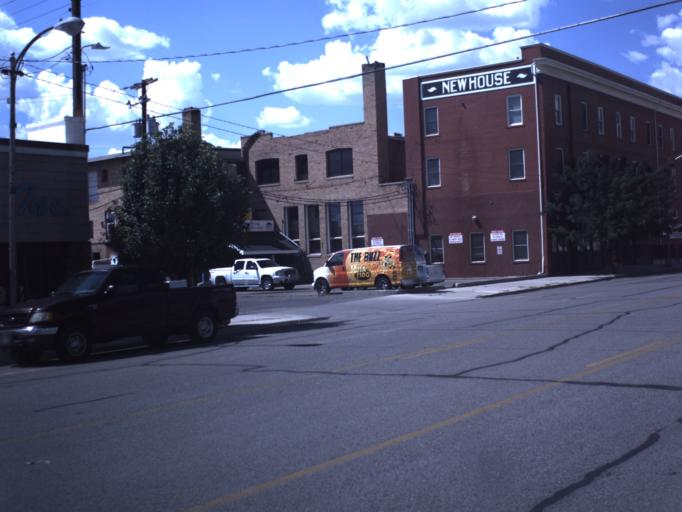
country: US
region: Utah
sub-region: Carbon County
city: Price
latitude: 39.5987
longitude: -110.8112
